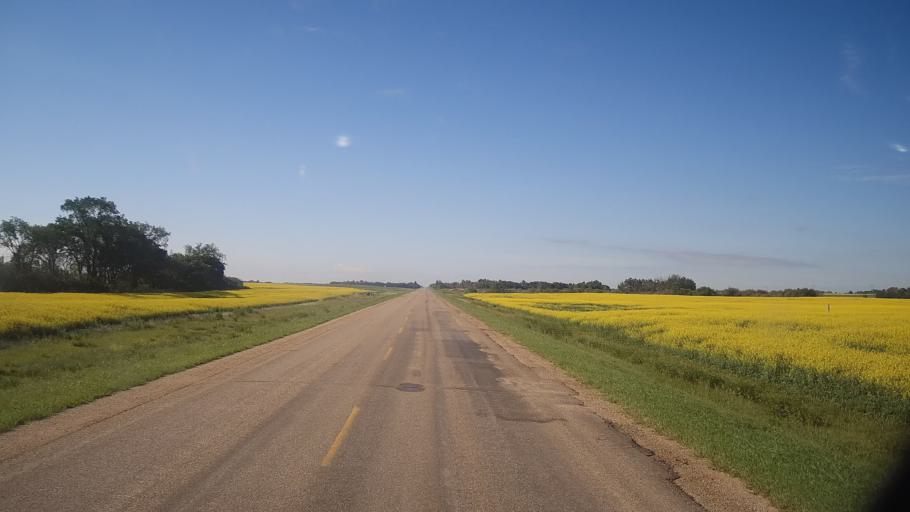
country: CA
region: Saskatchewan
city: Watrous
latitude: 51.8134
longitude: -105.2867
